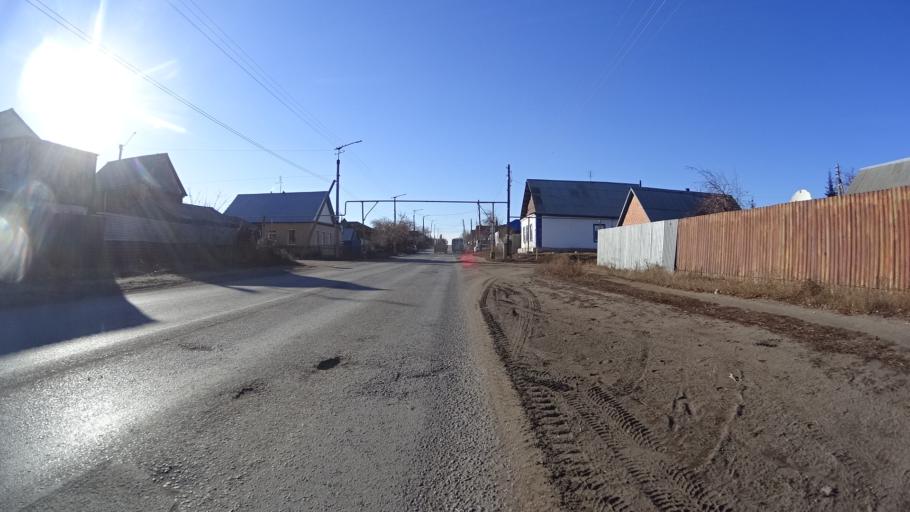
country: RU
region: Chelyabinsk
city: Troitsk
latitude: 54.0871
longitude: 61.5311
